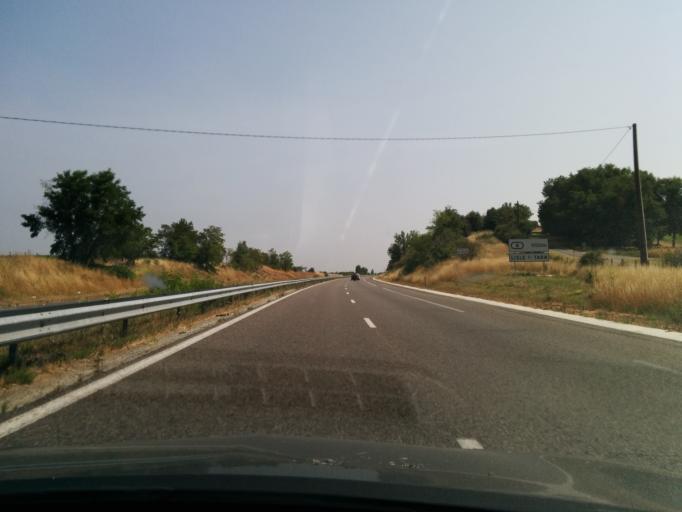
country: FR
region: Midi-Pyrenees
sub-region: Departement du Tarn
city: Lisle-sur-Tarn
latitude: 43.8342
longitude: 1.8323
